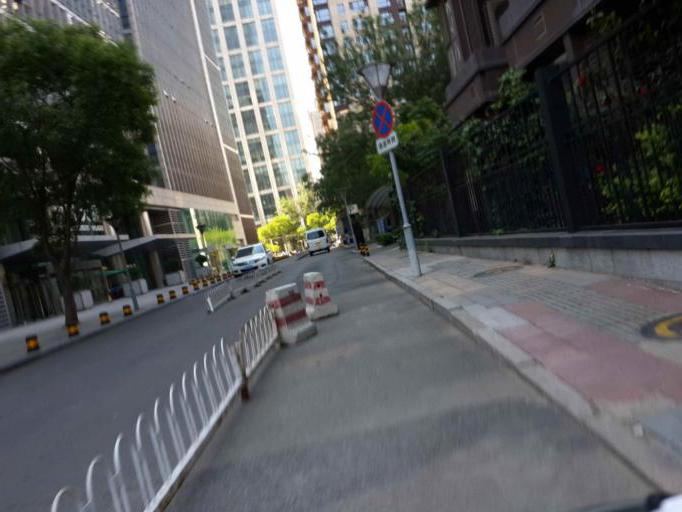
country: CN
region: Beijing
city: Chaowai
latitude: 39.9286
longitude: 116.4534
